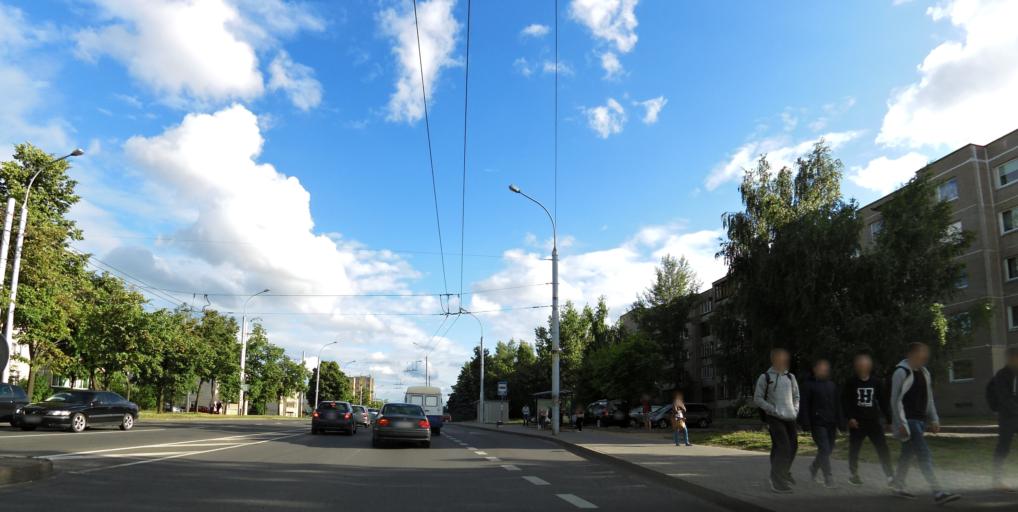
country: LT
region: Vilnius County
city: Rasos
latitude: 54.7112
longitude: 25.3047
